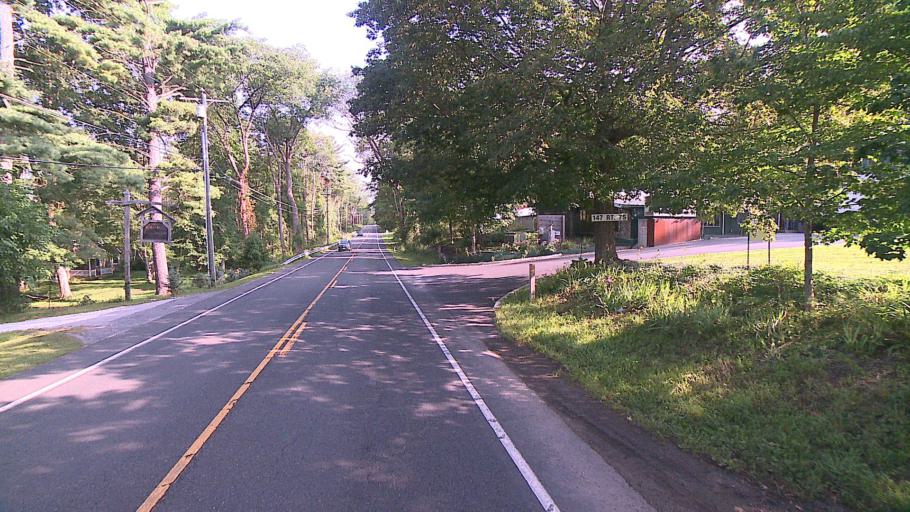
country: US
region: Connecticut
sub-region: Litchfield County
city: Canaan
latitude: 41.9464
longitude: -73.3596
